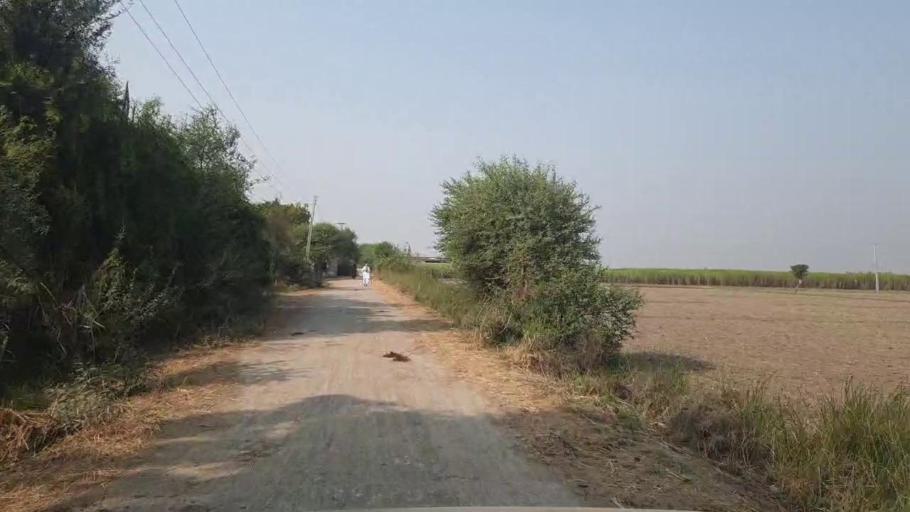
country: PK
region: Sindh
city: Tando Muhammad Khan
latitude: 25.0557
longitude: 68.3654
